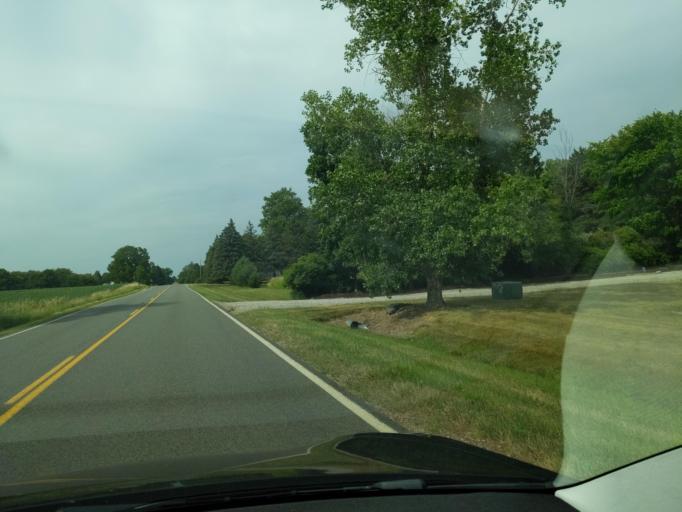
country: US
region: Michigan
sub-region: Clinton County
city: DeWitt
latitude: 42.8889
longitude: -84.6023
